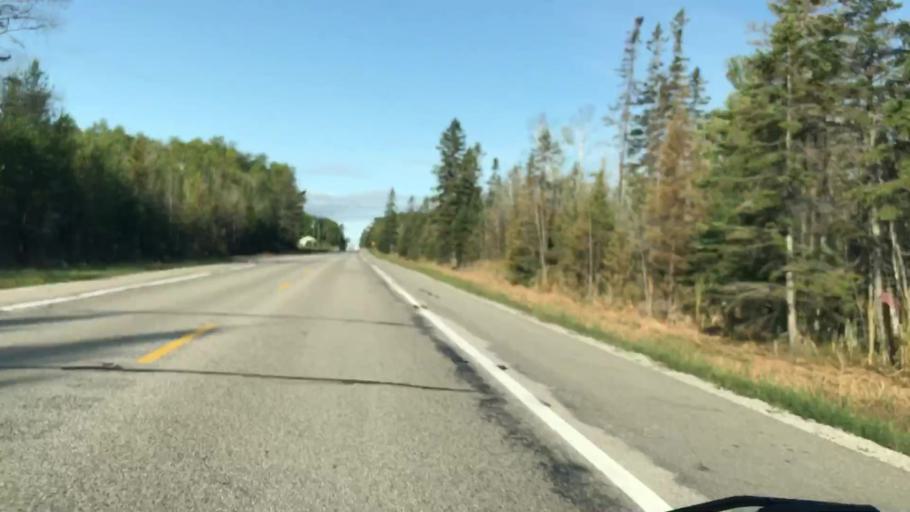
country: US
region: Michigan
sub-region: Luce County
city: Newberry
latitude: 46.3035
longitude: -85.3428
